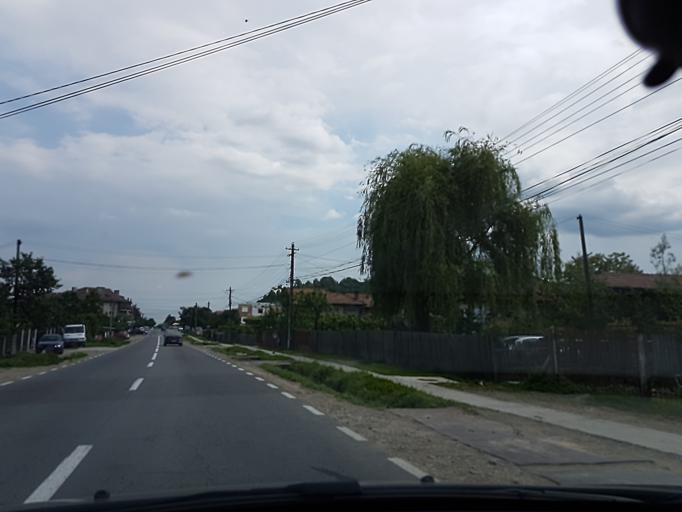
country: RO
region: Prahova
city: Maneciu
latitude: 45.3180
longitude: 25.9864
